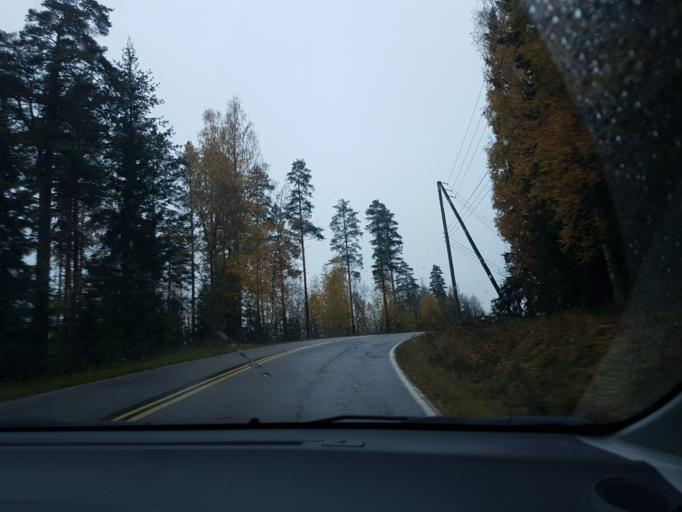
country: FI
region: Uusimaa
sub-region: Helsinki
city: Jaervenpaeae
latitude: 60.5785
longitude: 25.1612
